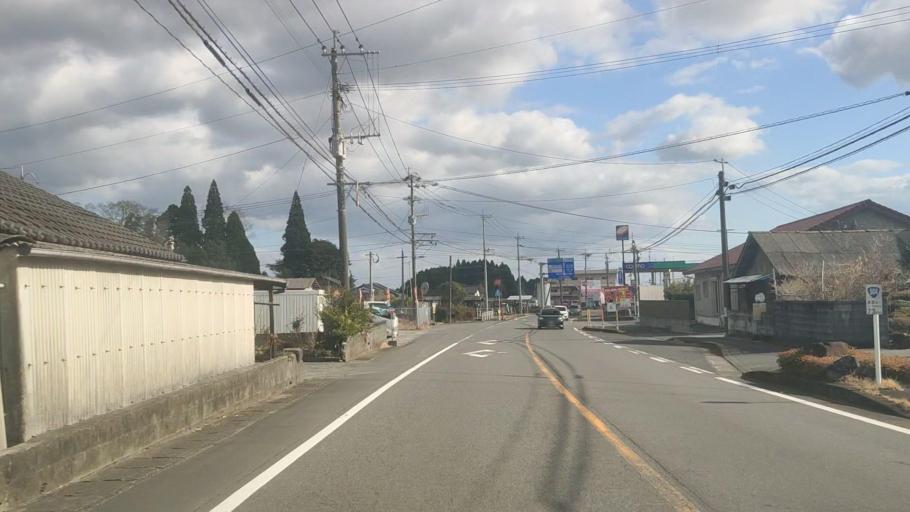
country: JP
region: Kagoshima
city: Kajiki
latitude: 31.8198
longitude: 130.7022
